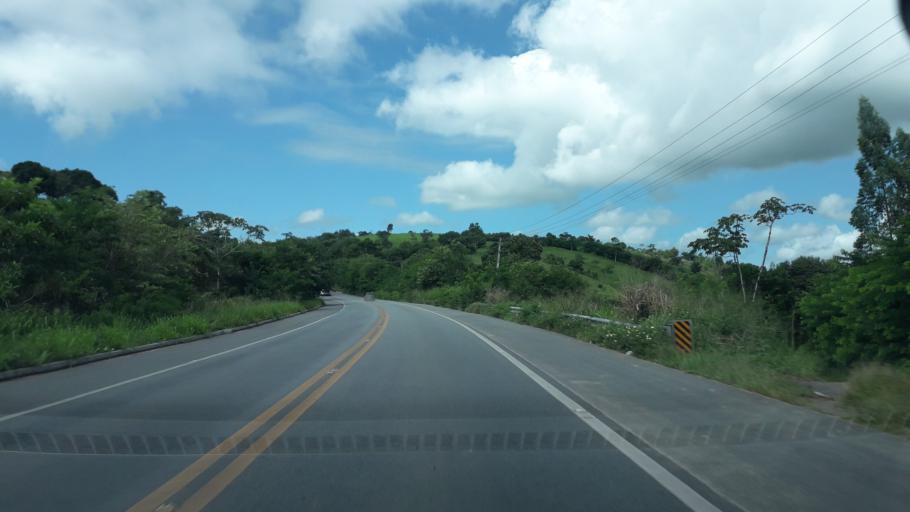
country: BR
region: Alagoas
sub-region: Uniao Dos Palmares
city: Uniao dos Palmares
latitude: -9.2197
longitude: -36.0319
